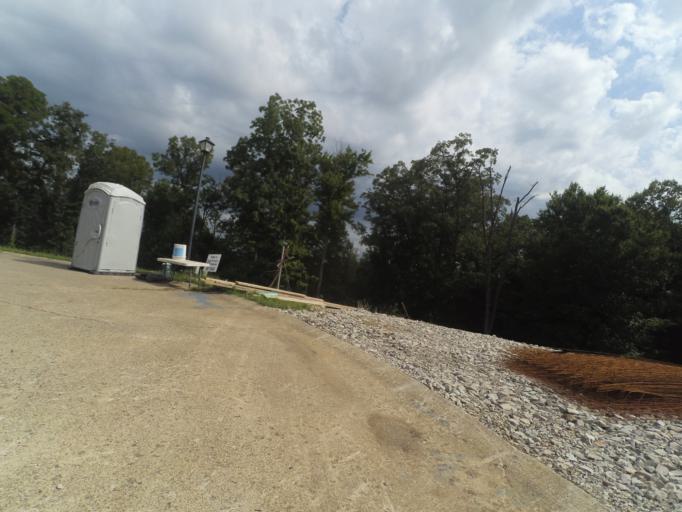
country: US
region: West Virginia
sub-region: Cabell County
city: Huntington
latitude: 38.3992
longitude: -82.4127
